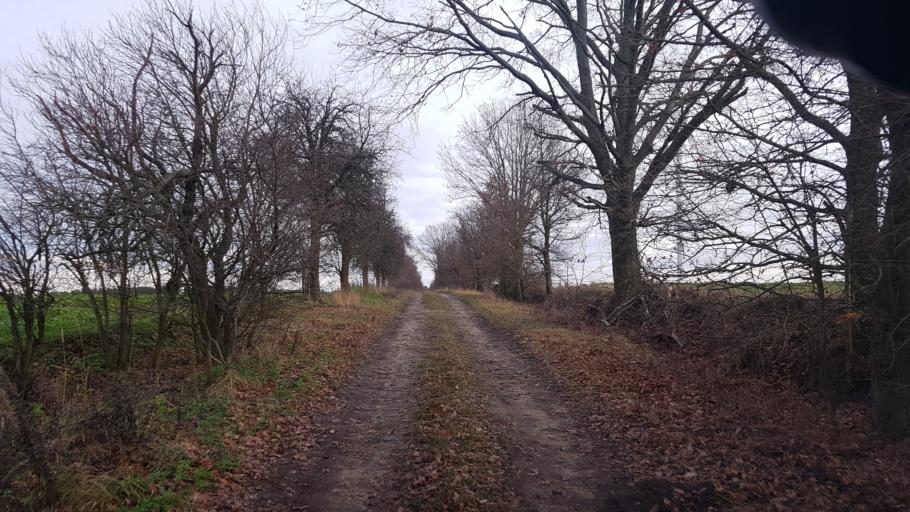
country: DE
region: Brandenburg
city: Hohenbucko
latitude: 51.7053
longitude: 13.4982
